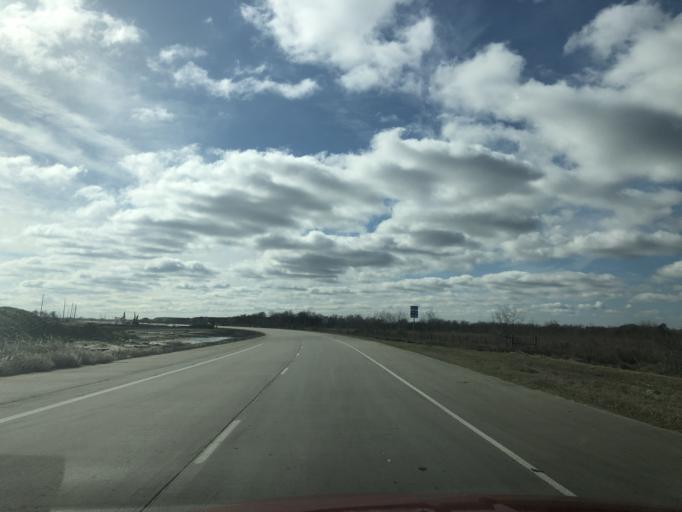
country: US
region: Texas
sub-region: Chambers County
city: Mont Belvieu
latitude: 29.8036
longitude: -94.8685
